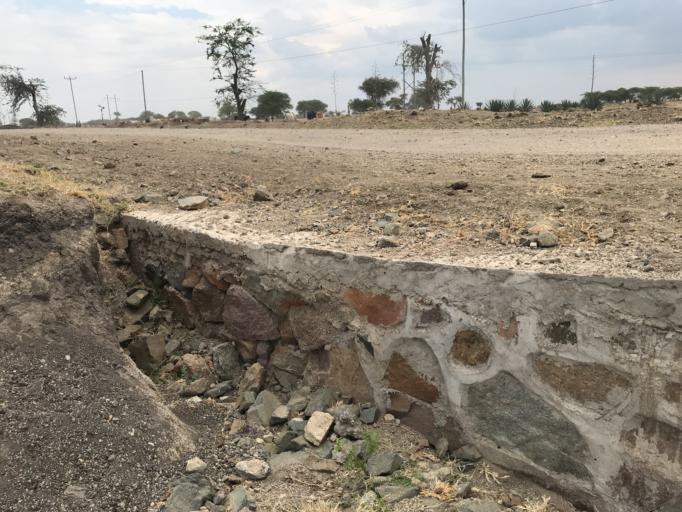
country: TZ
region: Mara
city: Bunda
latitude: -2.0795
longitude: 33.7029
